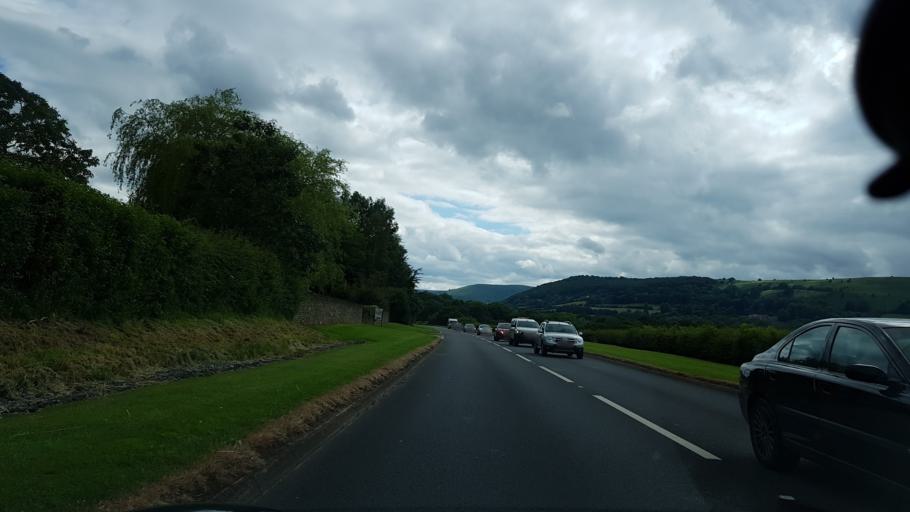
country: GB
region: Wales
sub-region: Monmouthshire
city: Abergavenny
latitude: 51.8615
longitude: -2.9964
